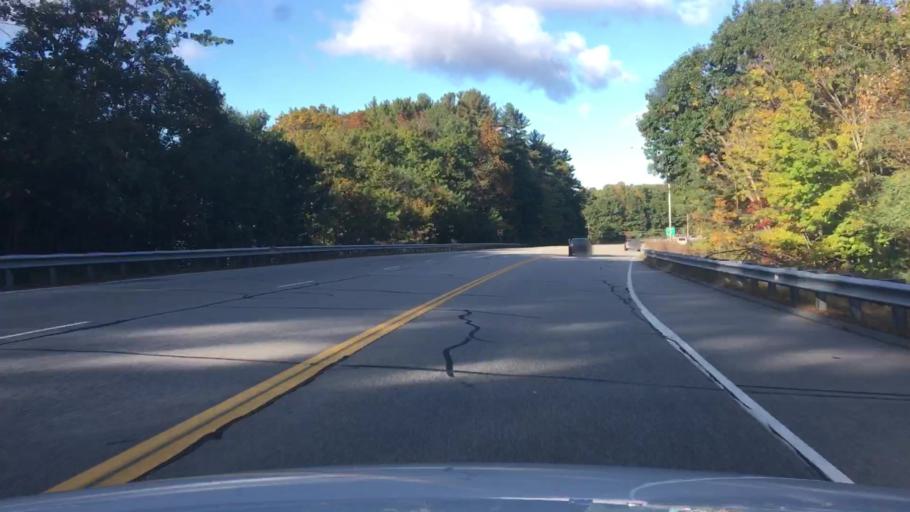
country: US
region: New Hampshire
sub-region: Strafford County
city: Durham
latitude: 43.1376
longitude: -70.9067
